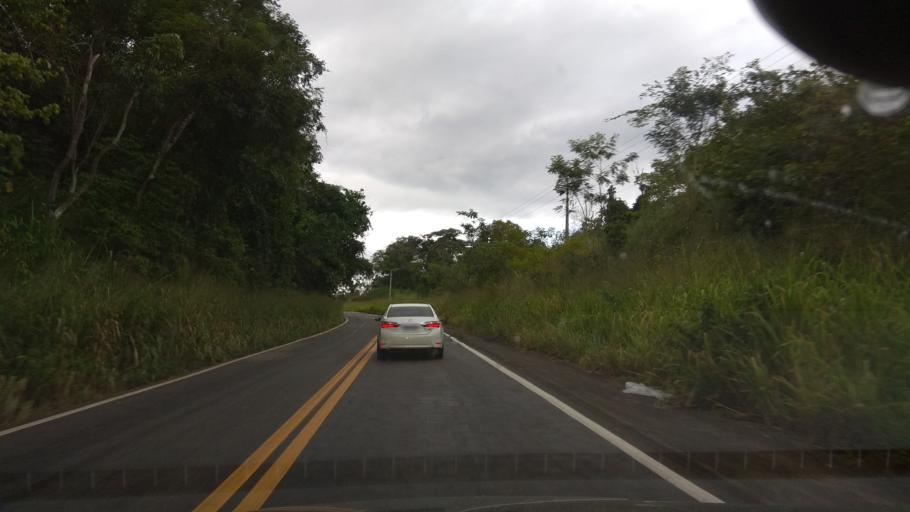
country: BR
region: Bahia
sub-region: Ubata
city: Ubata
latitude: -14.2305
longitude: -39.4535
